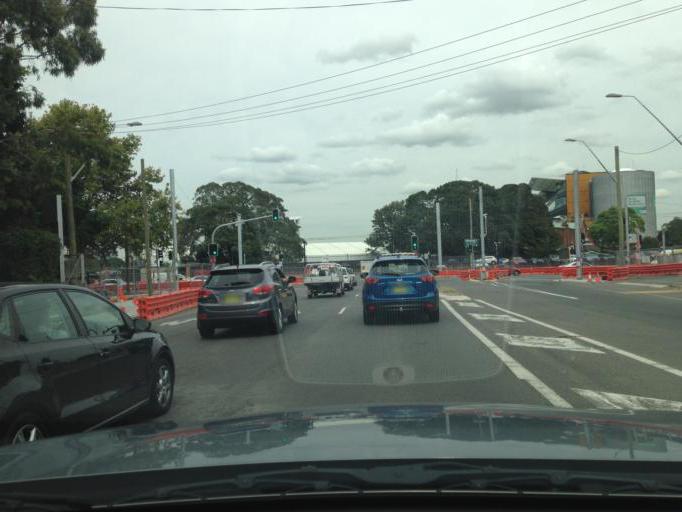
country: AU
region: New South Wales
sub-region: Randwick
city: Kensington
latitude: -33.9057
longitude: 151.2316
